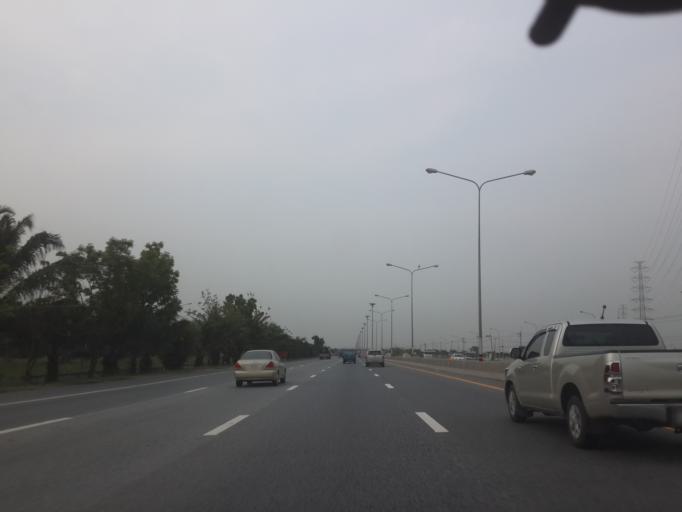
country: TH
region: Chon Buri
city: Phan Thong
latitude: 13.4497
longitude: 101.0460
